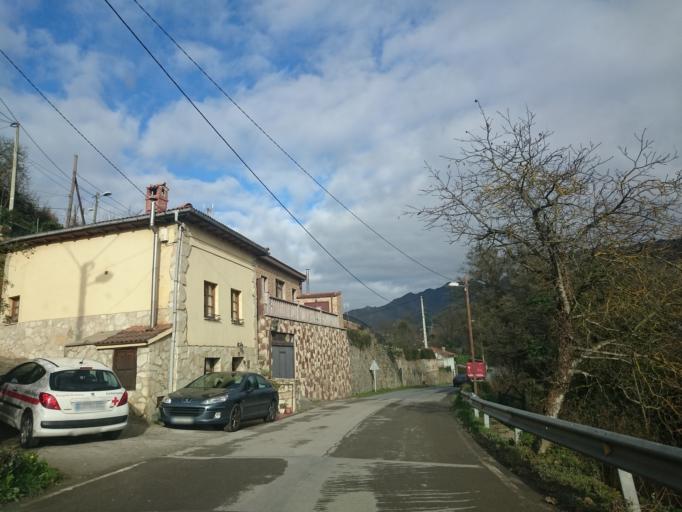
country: ES
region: Asturias
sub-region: Province of Asturias
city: Pola de Lena
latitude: 43.1071
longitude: -5.8202
